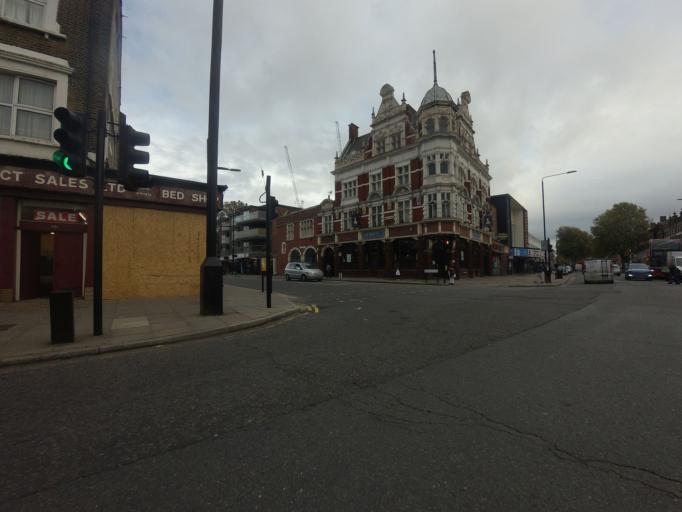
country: GB
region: England
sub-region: Greater London
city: East Ham
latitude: 51.5302
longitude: 0.0378
